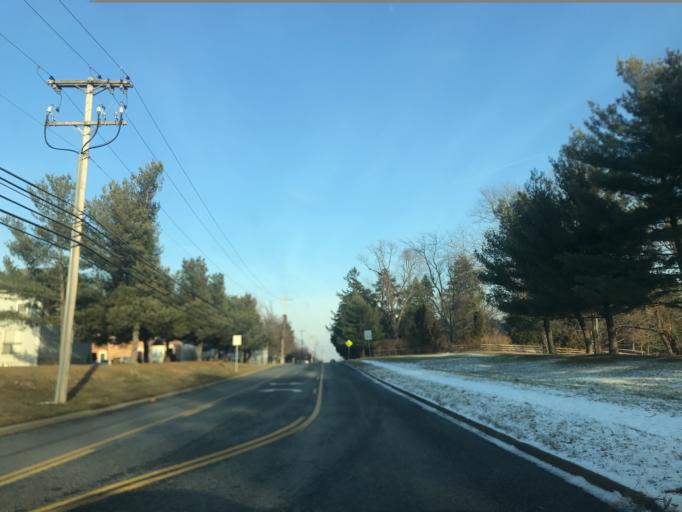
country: US
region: Maryland
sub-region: Harford County
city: Edgewood
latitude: 39.4235
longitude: -76.3193
